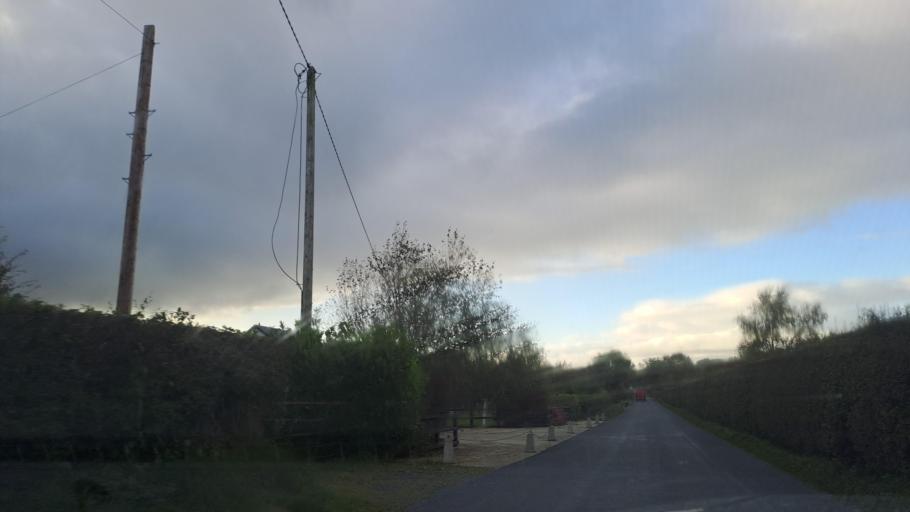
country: IE
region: Ulster
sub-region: County Monaghan
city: Carrickmacross
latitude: 54.0347
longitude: -6.8147
